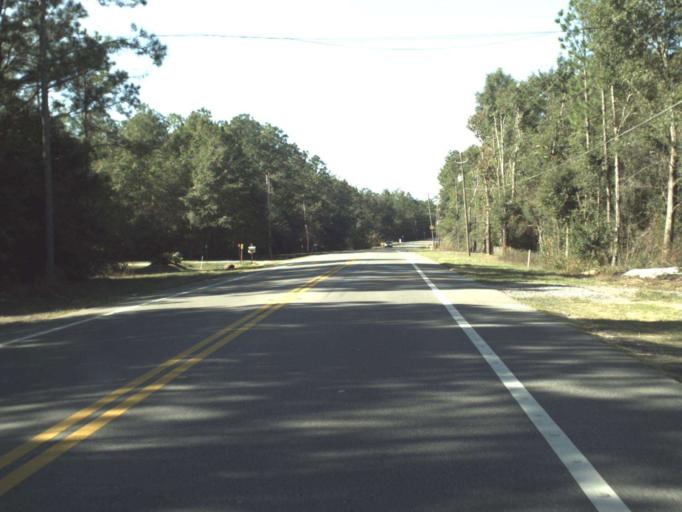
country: US
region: Florida
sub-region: Okaloosa County
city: Crestview
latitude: 30.7620
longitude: -86.6622
